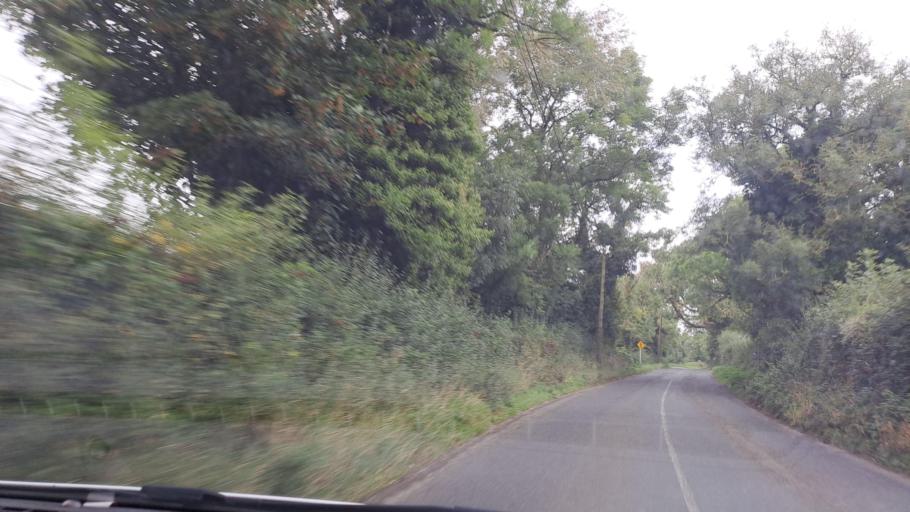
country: IE
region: Ulster
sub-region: County Monaghan
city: Carrickmacross
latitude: 53.8644
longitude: -6.6863
